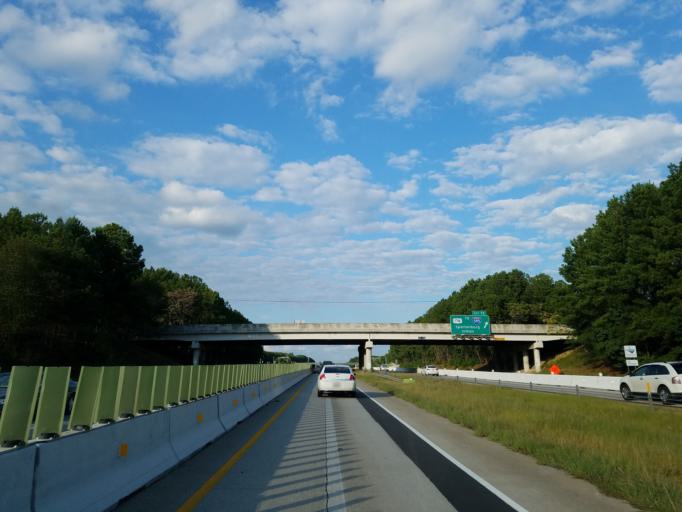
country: US
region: South Carolina
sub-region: Spartanburg County
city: Southern Shops
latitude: 34.9931
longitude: -81.9971
